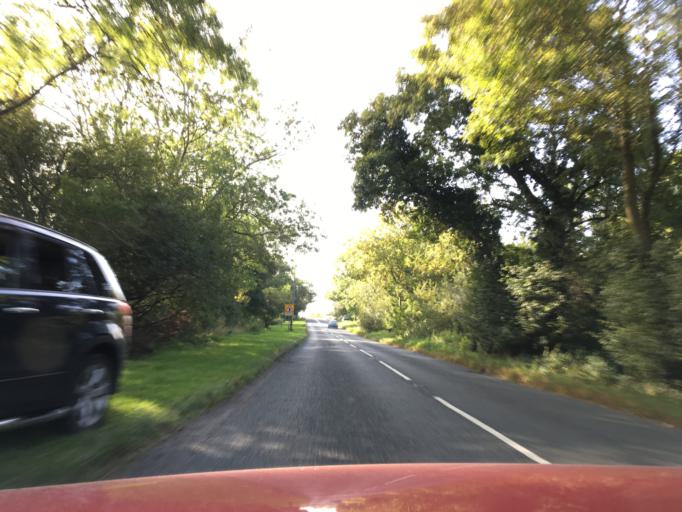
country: GB
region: England
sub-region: Gloucestershire
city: Tewkesbury
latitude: 51.9482
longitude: -2.2234
